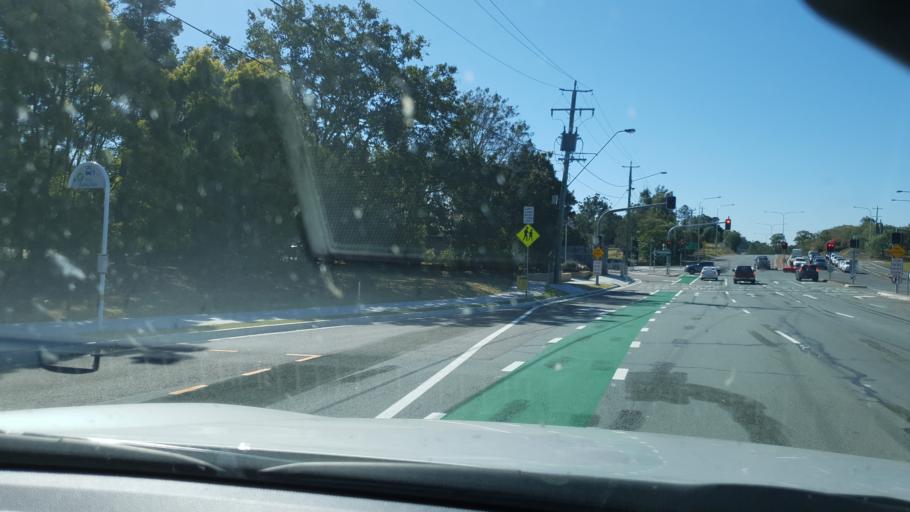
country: AU
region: Queensland
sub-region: Brisbane
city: Bridegman Downs
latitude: -27.3371
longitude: 152.9606
